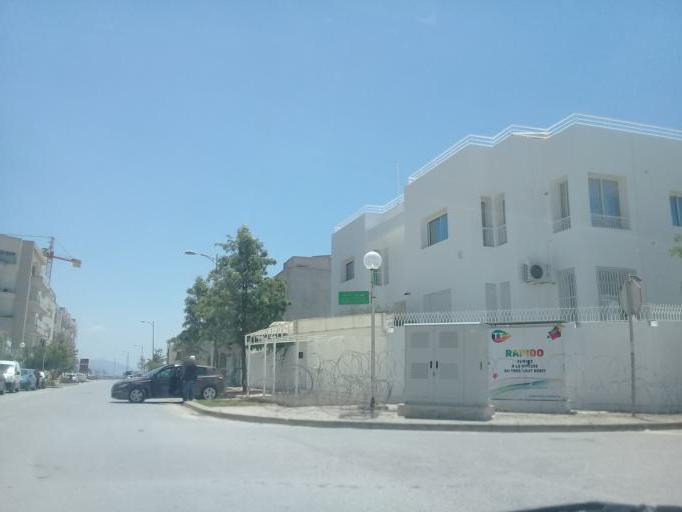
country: TN
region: Tunis
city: La Goulette
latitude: 36.8448
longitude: 10.2753
